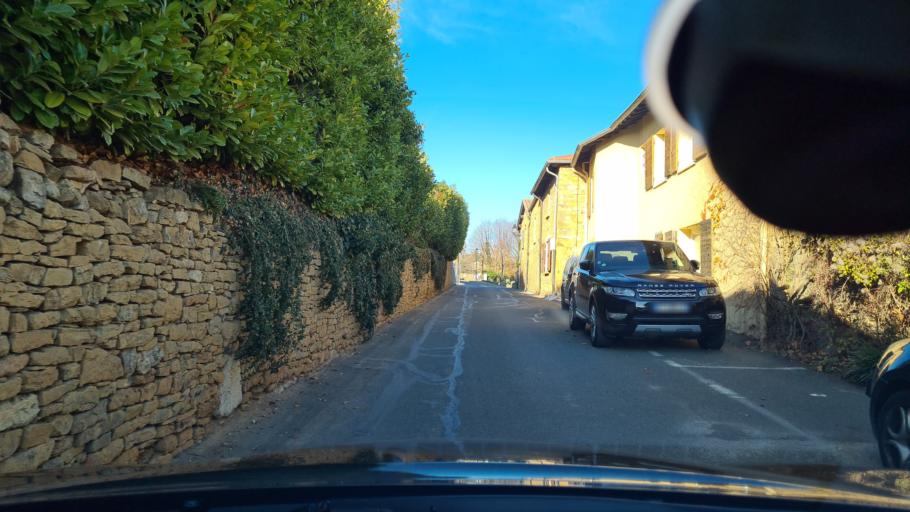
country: FR
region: Rhone-Alpes
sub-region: Departement du Rhone
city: Chasselay
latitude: 45.8605
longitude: 4.7984
